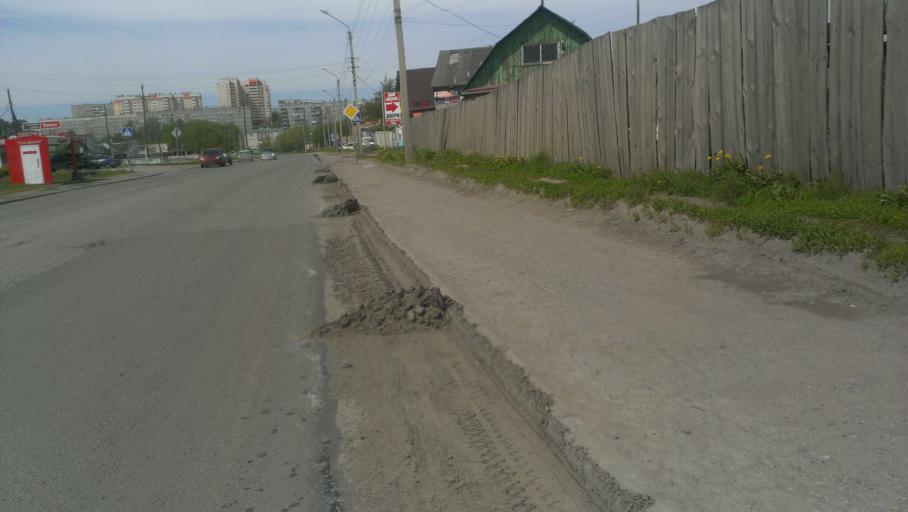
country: RU
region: Altai Krai
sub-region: Gorod Barnaulskiy
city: Barnaul
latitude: 53.3805
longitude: 83.6906
